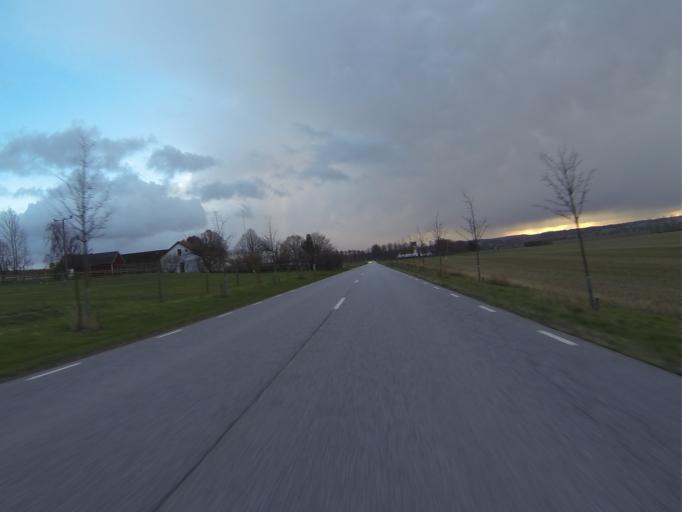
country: SE
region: Skane
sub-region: Lunds Kommun
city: Genarp
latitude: 55.6190
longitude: 13.4056
